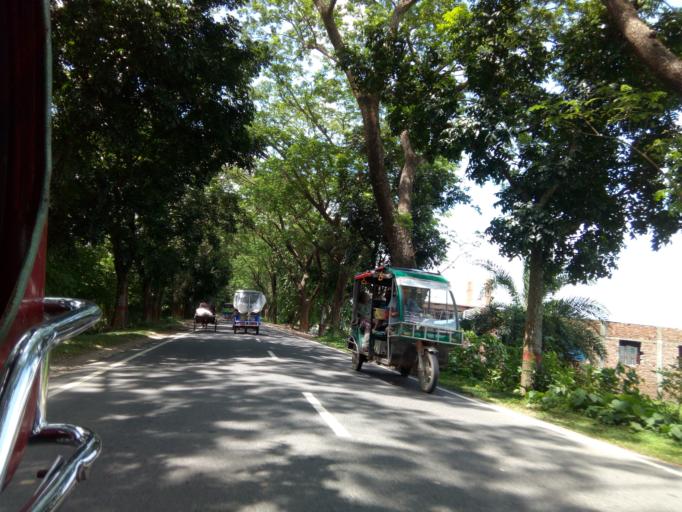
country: BD
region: Dhaka
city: Tungipara
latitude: 22.9709
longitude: 89.8130
